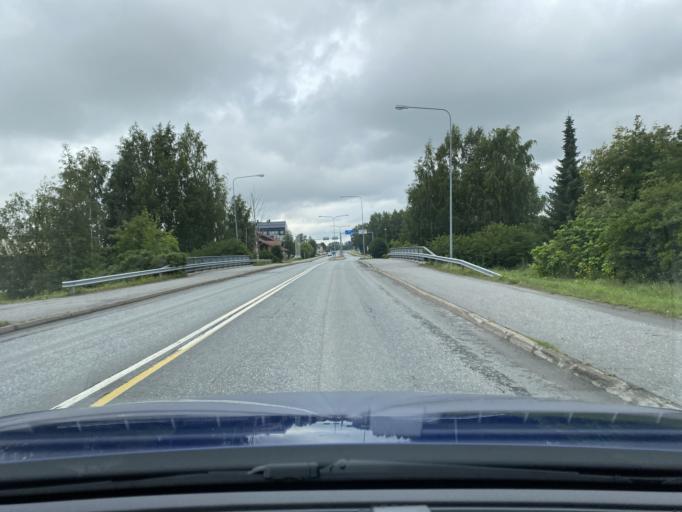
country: FI
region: Ostrobothnia
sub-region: Kyroenmaa
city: Laihia
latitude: 62.9789
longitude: 22.0118
